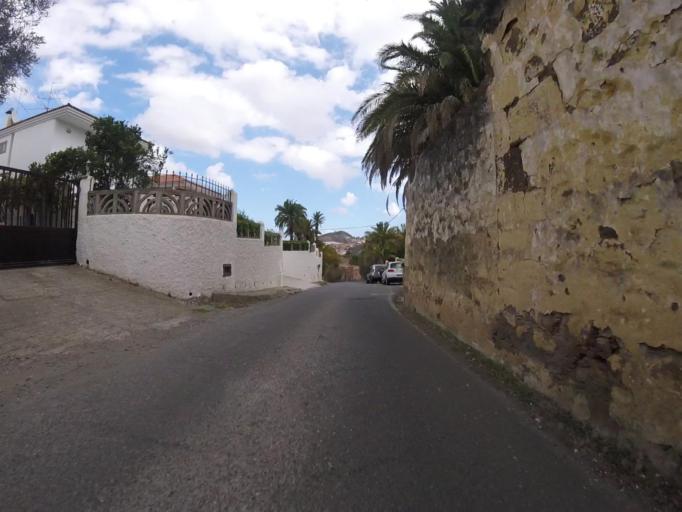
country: ES
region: Canary Islands
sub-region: Provincia de Las Palmas
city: Santa Brigida
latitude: 28.0442
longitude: -15.4880
